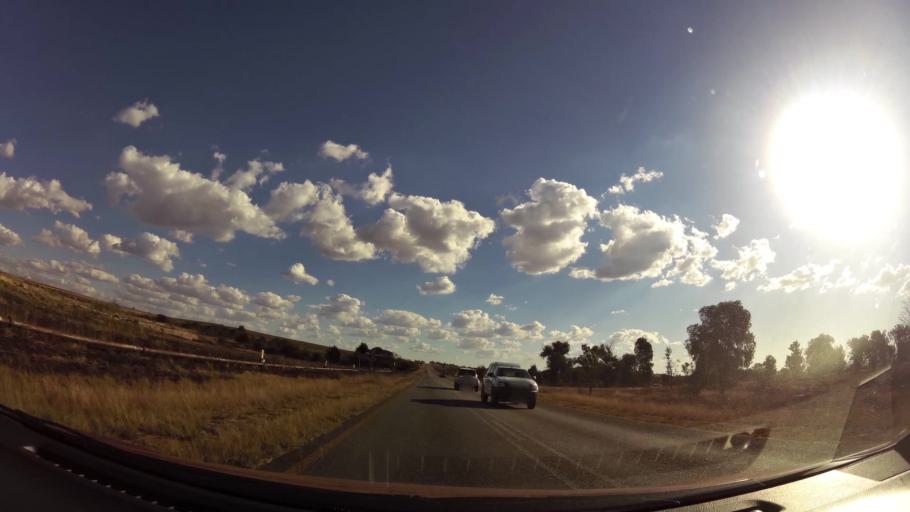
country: ZA
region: Gauteng
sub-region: West Rand District Municipality
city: Carletonville
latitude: -26.3840
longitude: 27.3632
